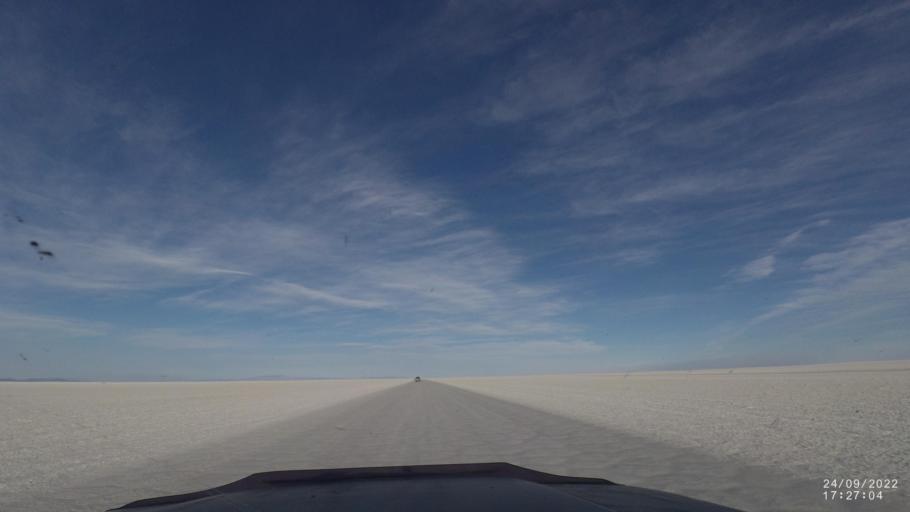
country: BO
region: Potosi
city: Colchani
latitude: -20.2985
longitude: -67.4564
